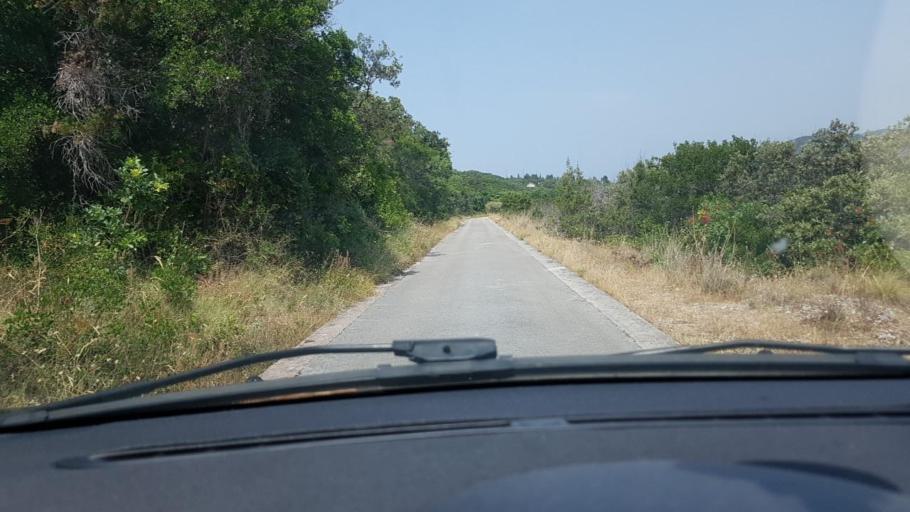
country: ME
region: Herceg Novi
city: Herceg-Novi
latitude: 42.3962
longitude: 18.5267
